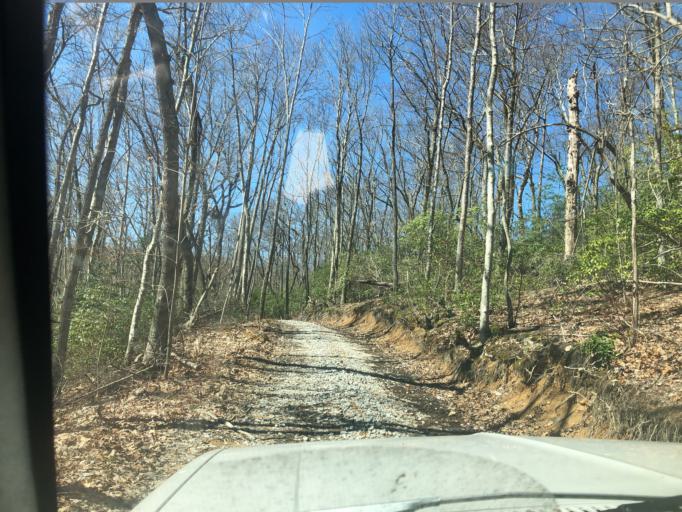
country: US
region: Tennessee
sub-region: Cumberland County
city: Fairfield Glade
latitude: 35.9711
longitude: -84.7602
